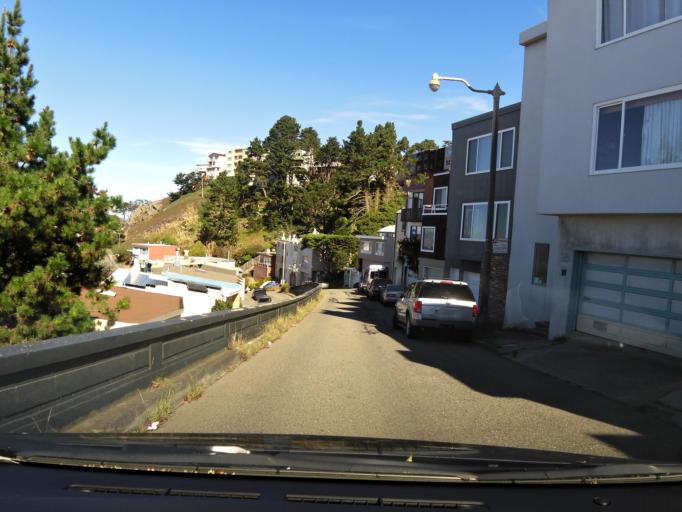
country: US
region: California
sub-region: San Mateo County
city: Daly City
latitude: 37.7513
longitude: -122.4707
